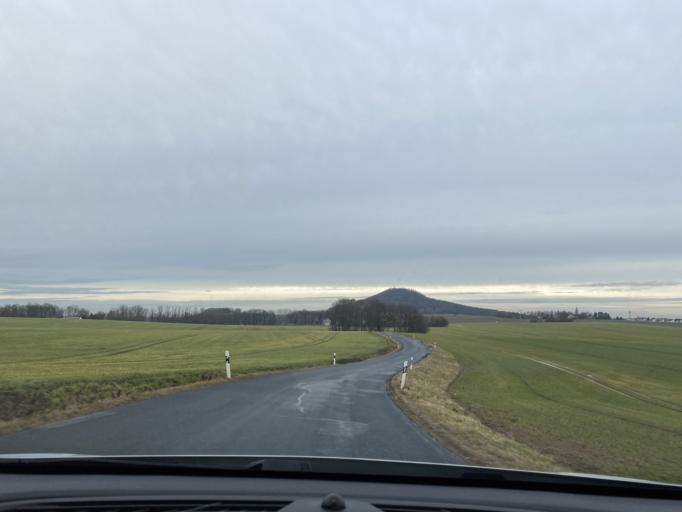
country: DE
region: Saxony
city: Markersdorf
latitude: 51.1056
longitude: 14.9203
